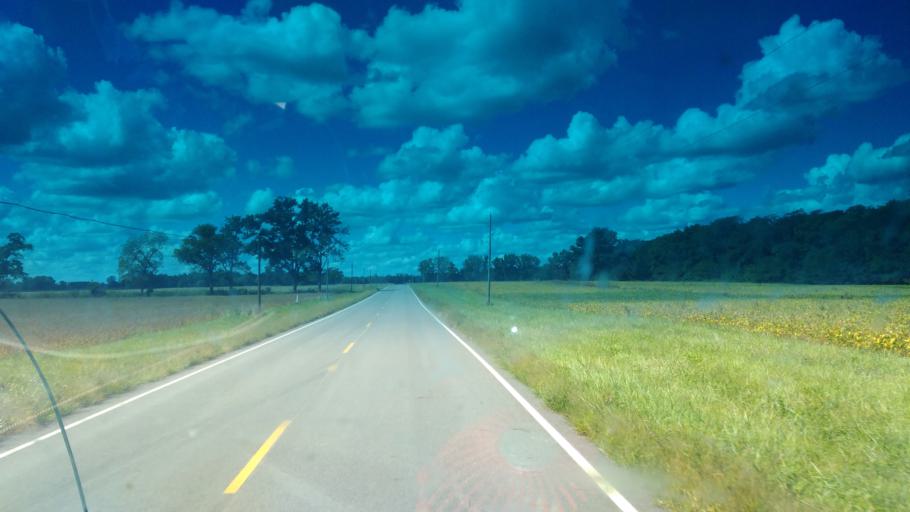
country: US
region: Ohio
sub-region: Champaign County
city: North Lewisburg
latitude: 40.2030
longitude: -83.4854
